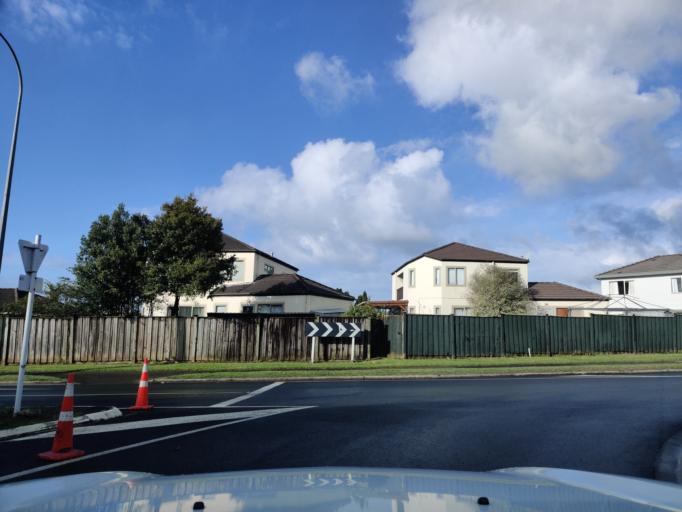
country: NZ
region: Auckland
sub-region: Auckland
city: Pakuranga
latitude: -36.9144
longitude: 174.9081
